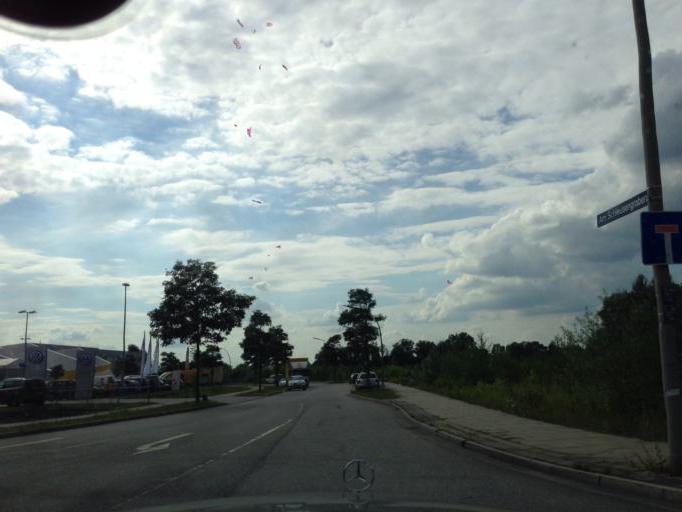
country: DE
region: Hamburg
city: Bergedorf
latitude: 53.4773
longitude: 10.2061
